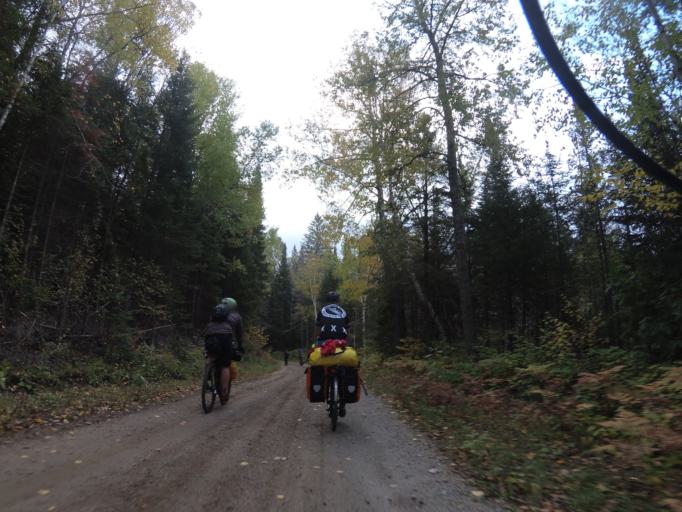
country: CA
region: Ontario
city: Pembroke
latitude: 45.3022
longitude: -77.2574
